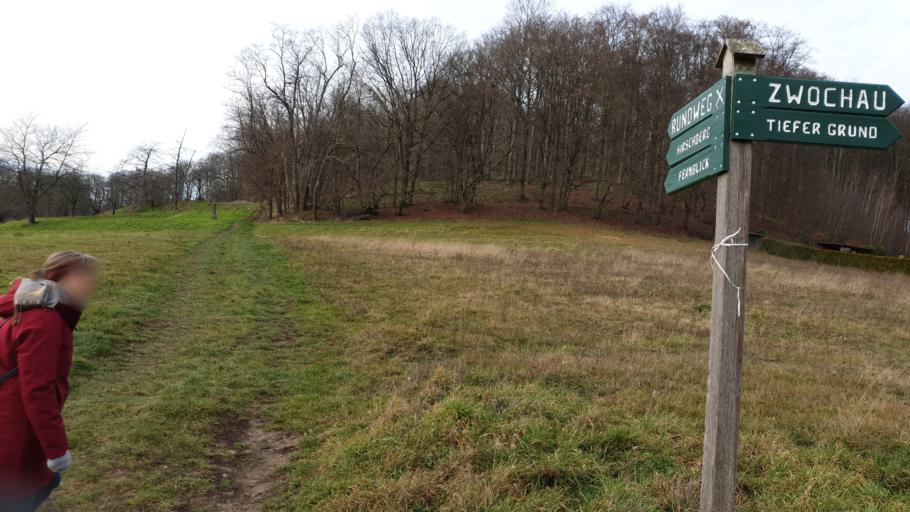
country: DE
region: Saxony
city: Hohburg
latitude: 51.4175
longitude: 12.8036
